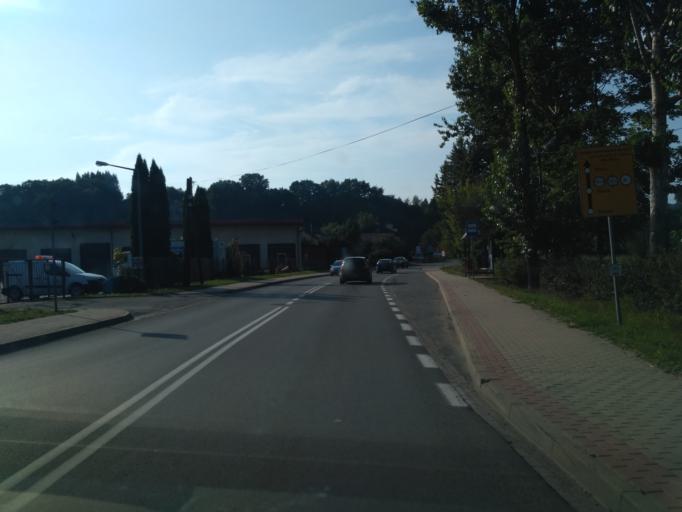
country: PL
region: Subcarpathian Voivodeship
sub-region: Powiat sanocki
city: Sanok
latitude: 49.5755
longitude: 22.1972
